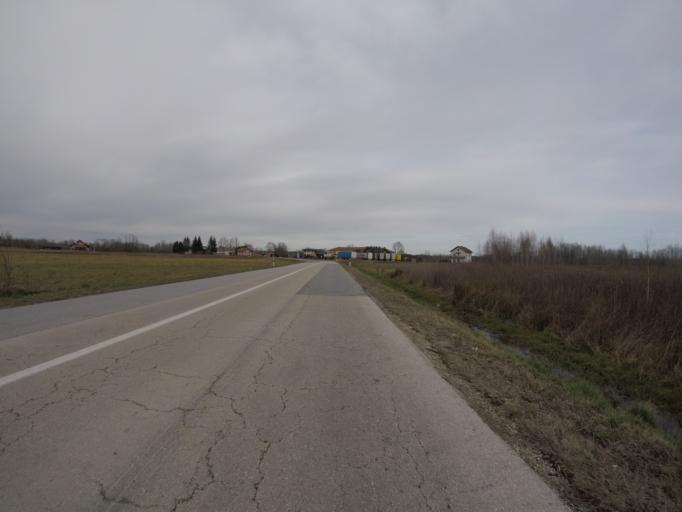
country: HR
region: Grad Zagreb
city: Horvati
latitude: 45.5653
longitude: 15.8635
